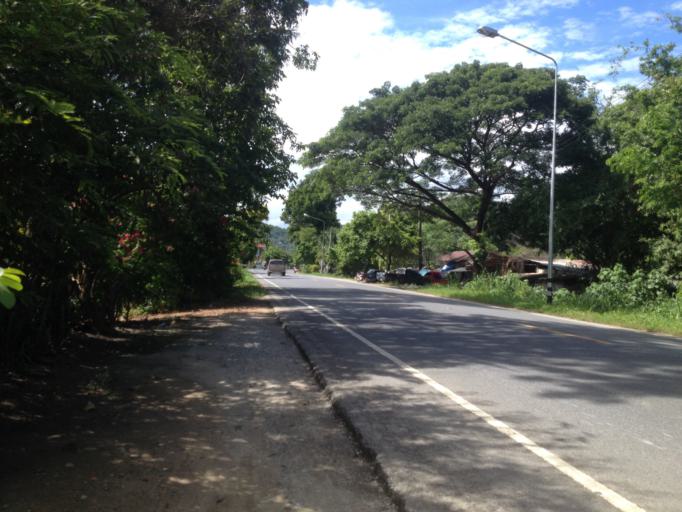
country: TH
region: Chiang Mai
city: Hang Dong
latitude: 18.7277
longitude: 98.9092
